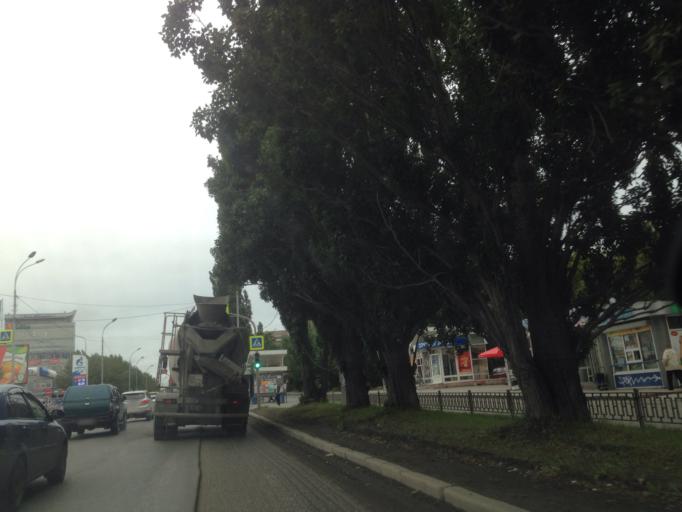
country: RU
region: Sverdlovsk
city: Yekaterinburg
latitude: 56.8359
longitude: 60.6338
